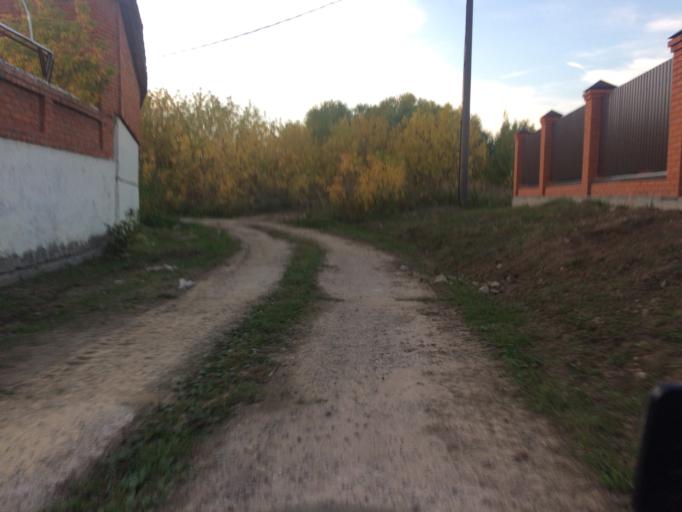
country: RU
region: Mariy-El
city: Yoshkar-Ola
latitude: 56.6444
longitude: 47.9159
